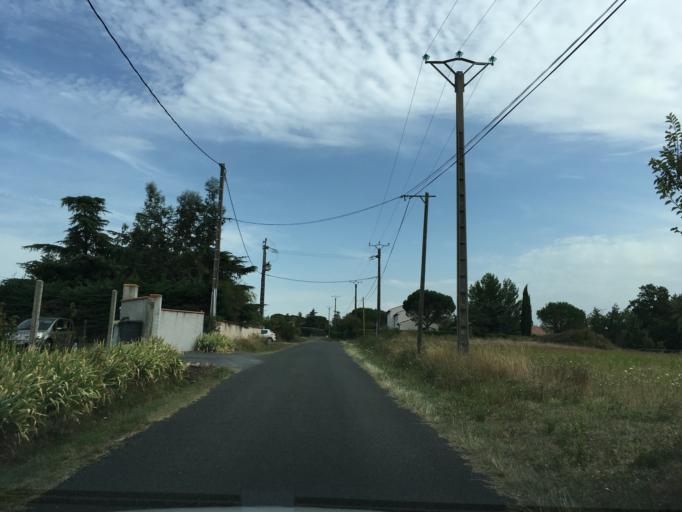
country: FR
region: Midi-Pyrenees
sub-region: Departement du Tarn
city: Lagarrigue
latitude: 43.6025
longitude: 2.2862
